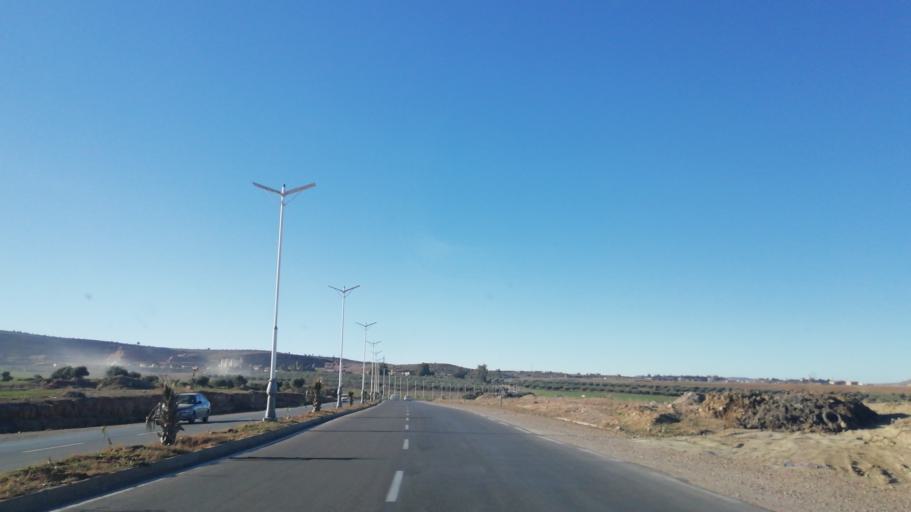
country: DZ
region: Saida
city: Saida
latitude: 34.8493
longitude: 0.1930
